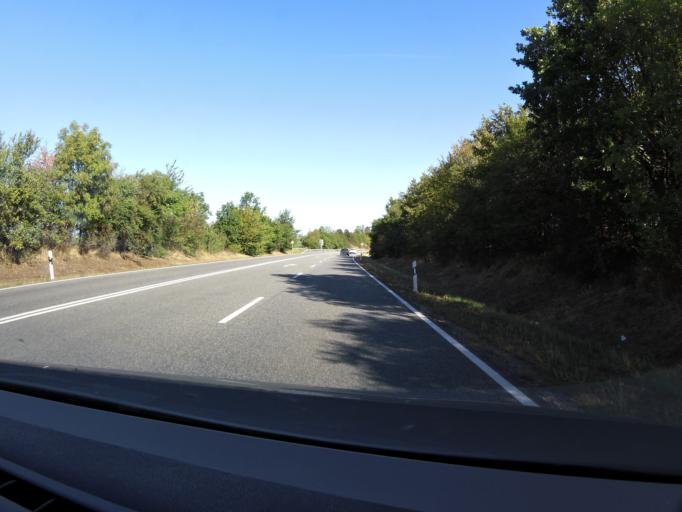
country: DE
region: Thuringia
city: Nordhausen
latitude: 51.4660
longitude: 10.8003
